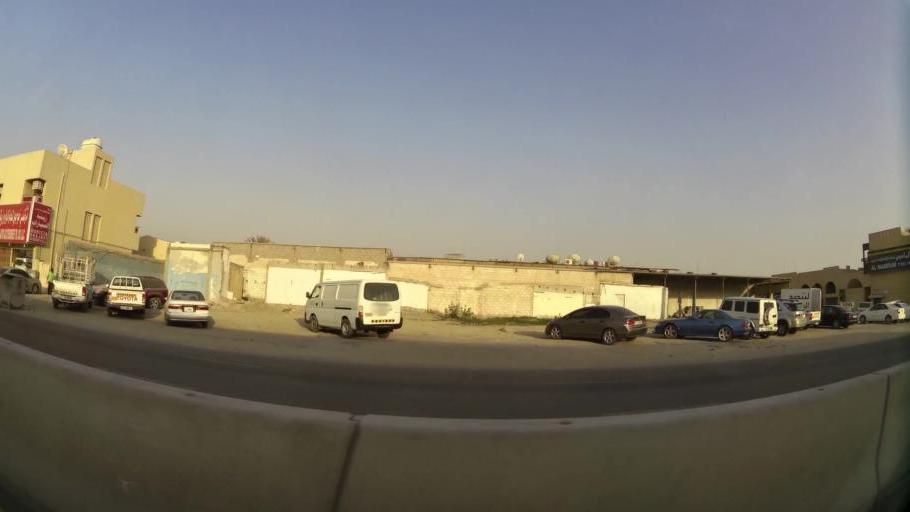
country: AE
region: Ash Shariqah
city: Sharjah
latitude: 25.3119
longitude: 55.3939
